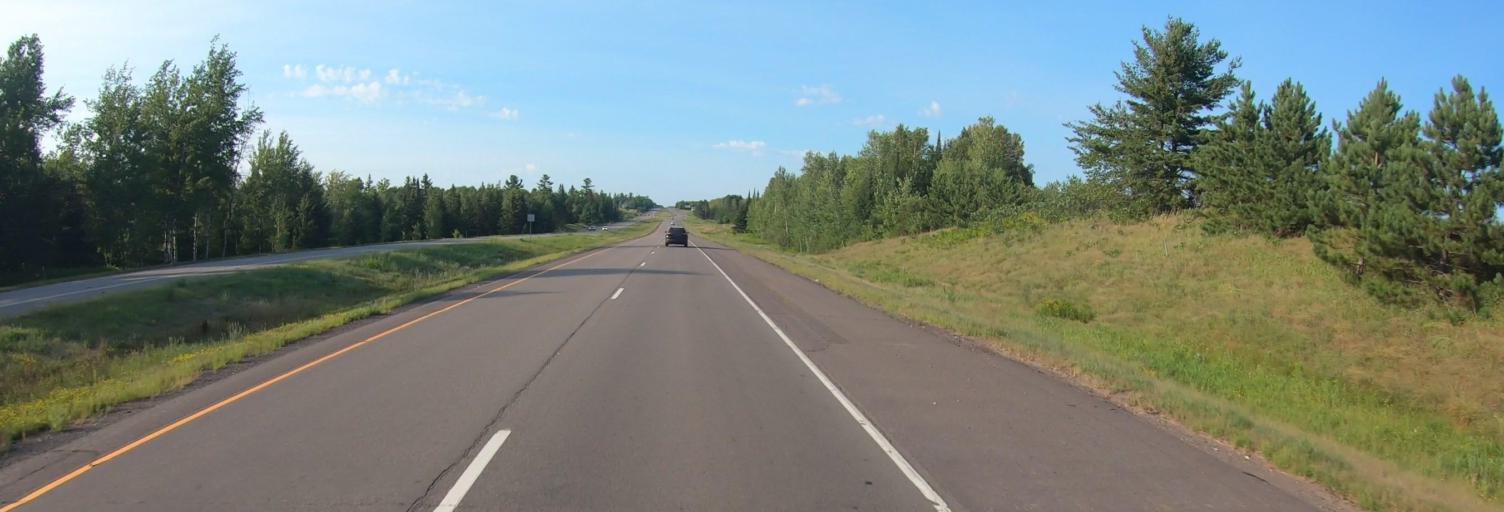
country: US
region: Minnesota
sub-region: Carlton County
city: Cloquet
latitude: 47.0197
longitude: -92.4707
